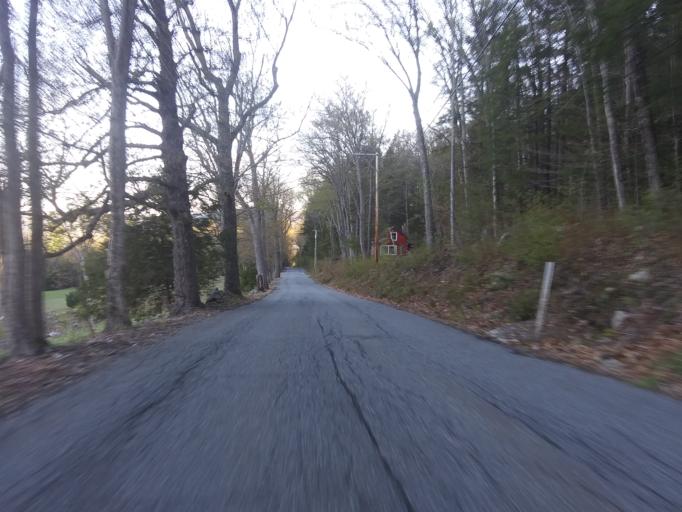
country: US
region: Massachusetts
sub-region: Franklin County
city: Shelburne Falls
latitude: 42.5996
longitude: -72.7597
